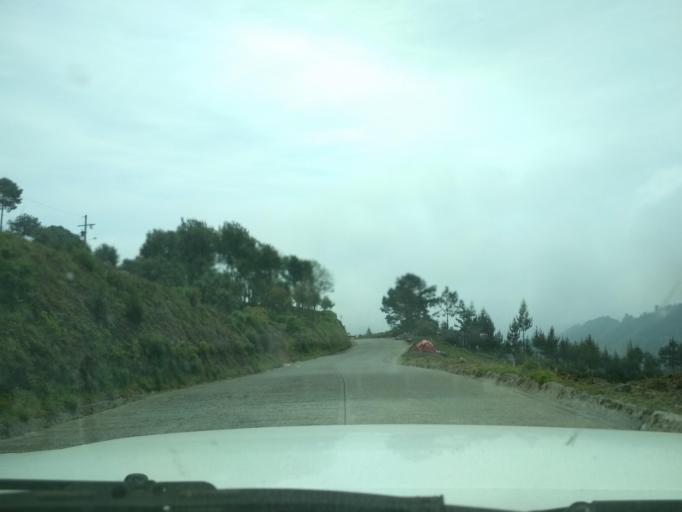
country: MX
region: Veracruz
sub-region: Mariano Escobedo
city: San Isidro el Berro
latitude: 18.9753
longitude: -97.2090
